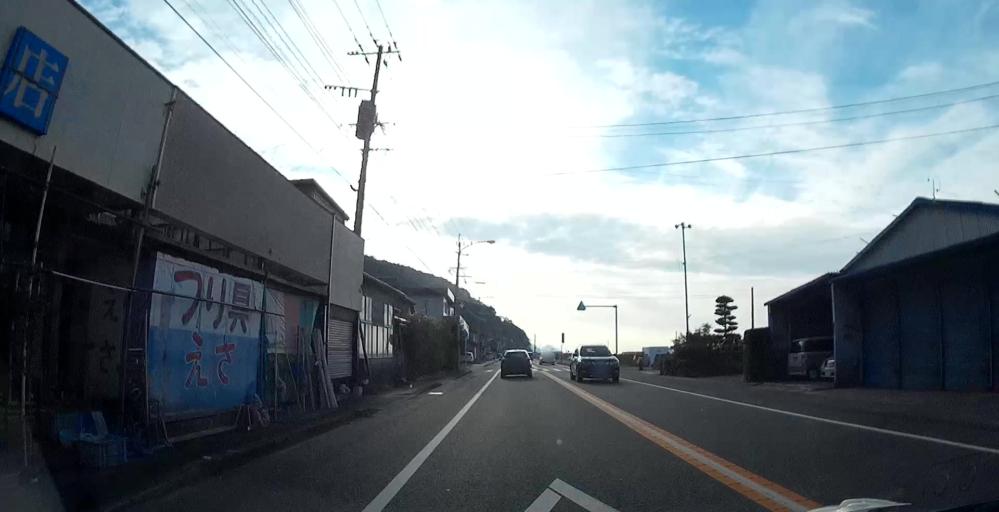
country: JP
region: Kumamoto
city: Uto
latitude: 32.6916
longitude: 130.5613
